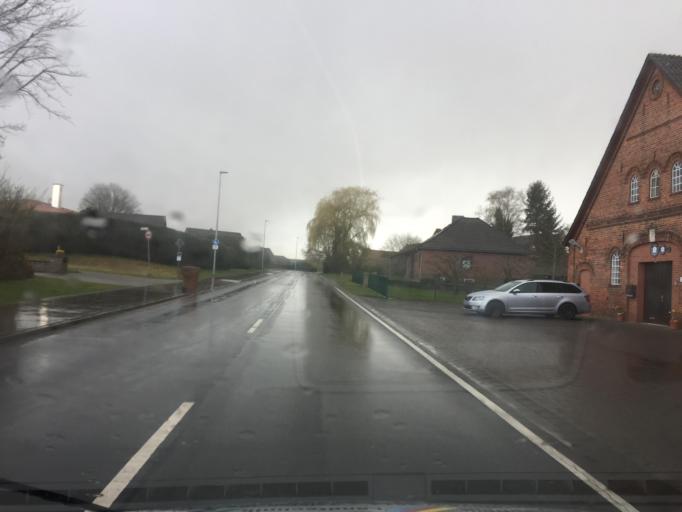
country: DE
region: Lower Saxony
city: Syke
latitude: 52.9337
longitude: 8.8849
